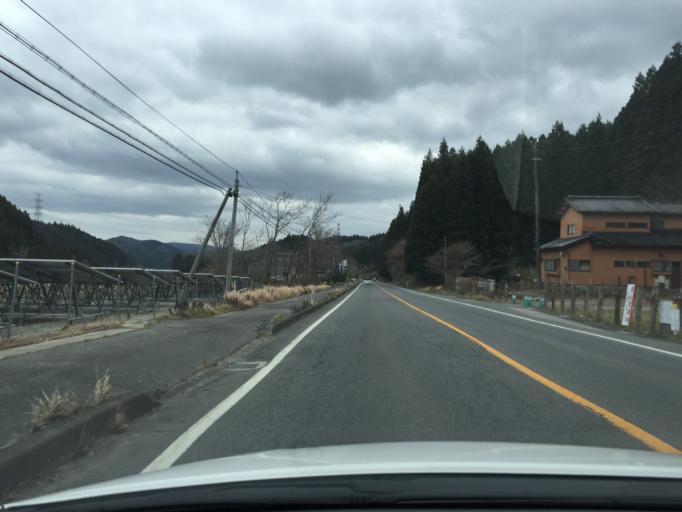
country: JP
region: Fukushima
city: Iwaki
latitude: 37.1400
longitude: 140.6898
